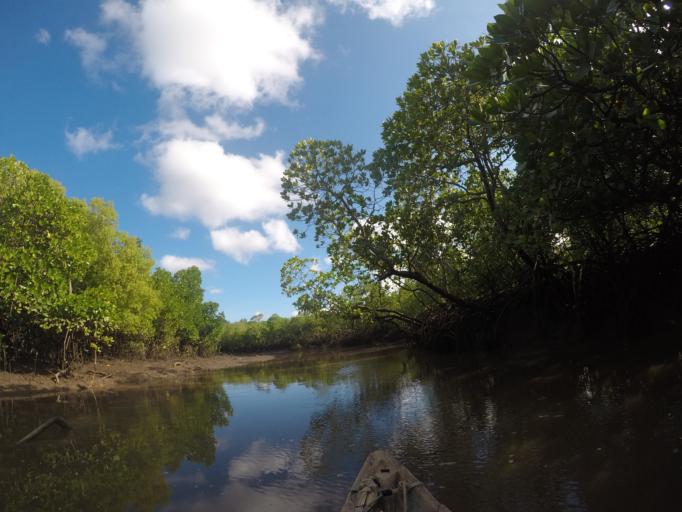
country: TZ
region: Pemba South
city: Mtambile
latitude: -5.3462
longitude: 39.6967
